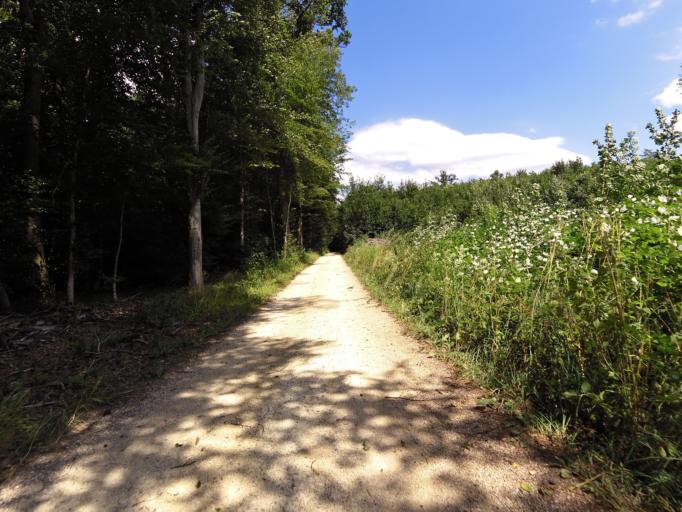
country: CH
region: Thurgau
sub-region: Kreuzlingen District
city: Tagerwilen
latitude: 47.6361
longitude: 9.1067
